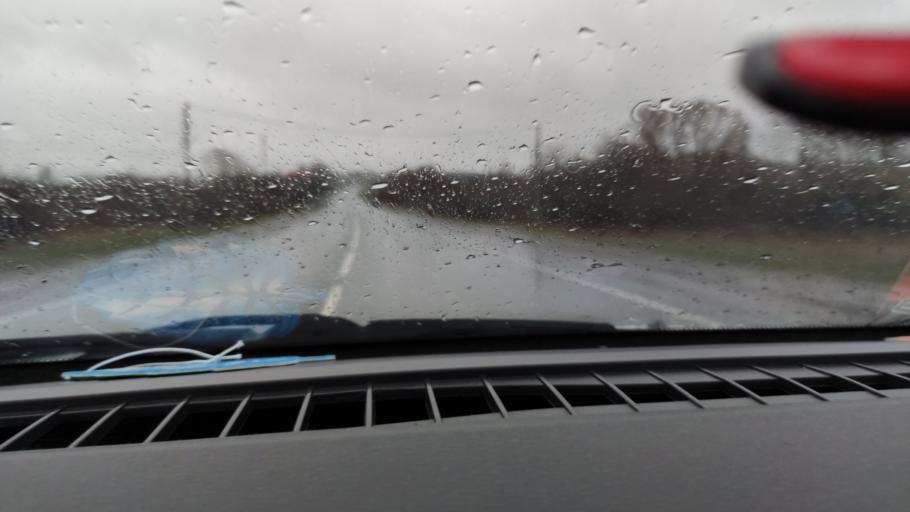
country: RU
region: Tatarstan
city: Mendeleyevsk
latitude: 55.8566
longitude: 52.2119
